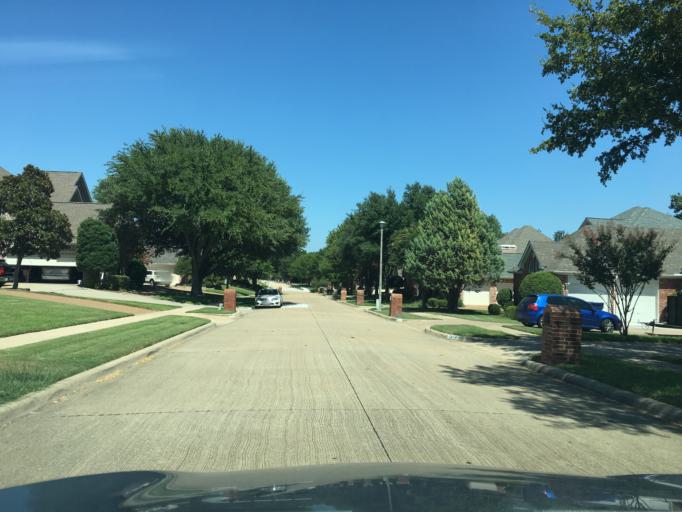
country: US
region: Texas
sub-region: Dallas County
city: Sachse
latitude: 32.9633
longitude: -96.6270
